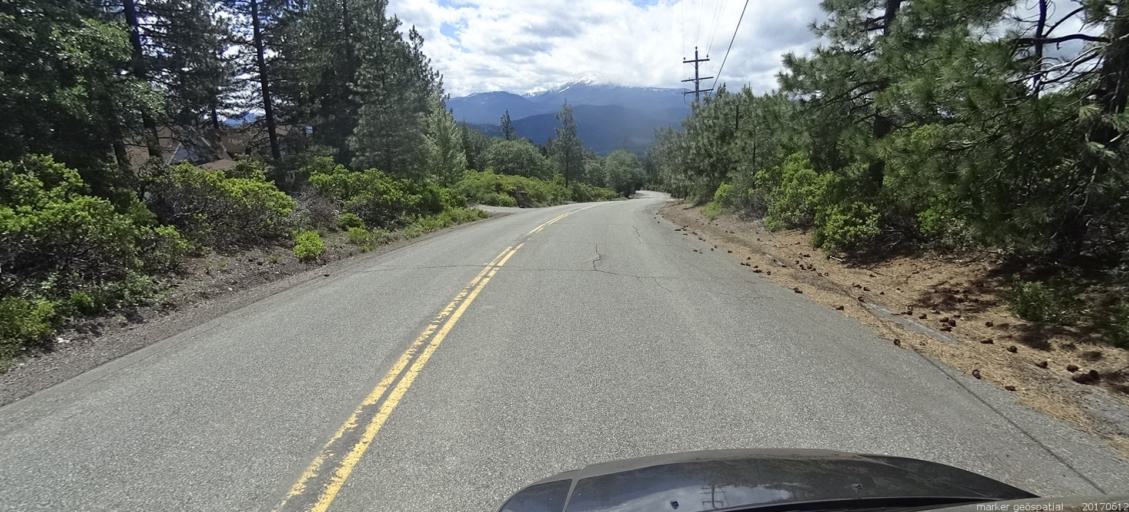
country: US
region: California
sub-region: Siskiyou County
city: Mount Shasta
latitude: 41.2987
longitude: -122.2882
